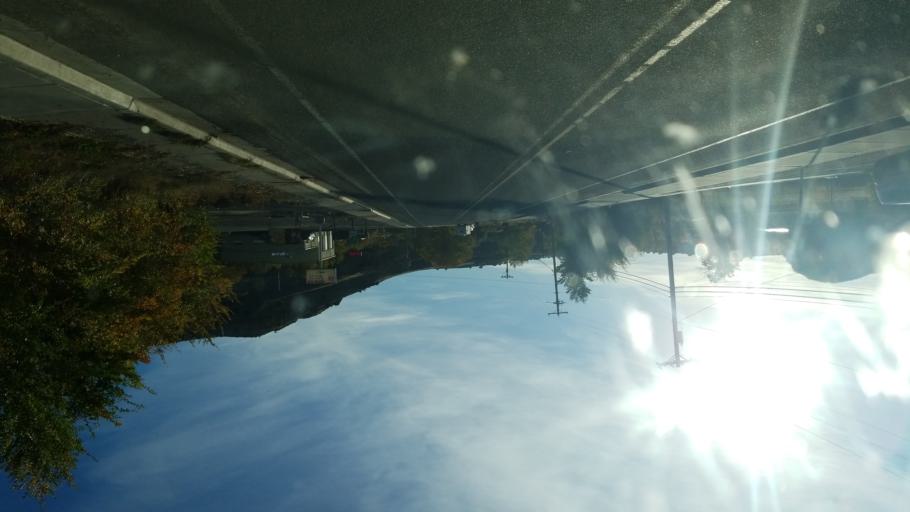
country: US
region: New Mexico
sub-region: San Juan County
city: Bloomfield
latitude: 36.7237
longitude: -107.8262
